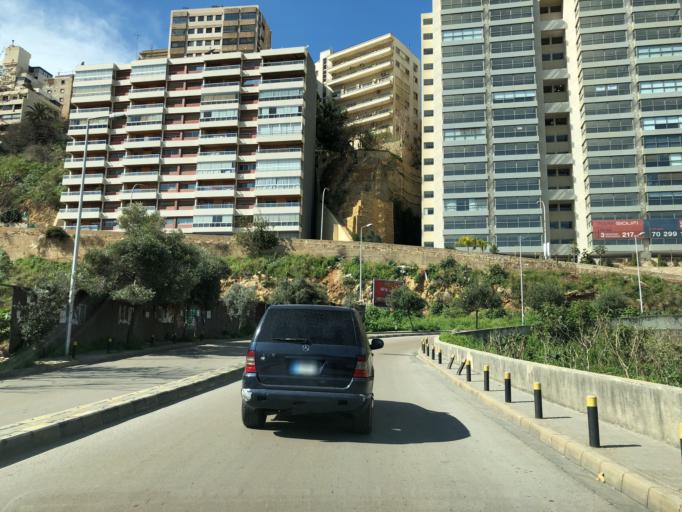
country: LB
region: Beyrouth
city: Beirut
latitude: 33.8847
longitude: 35.5302
